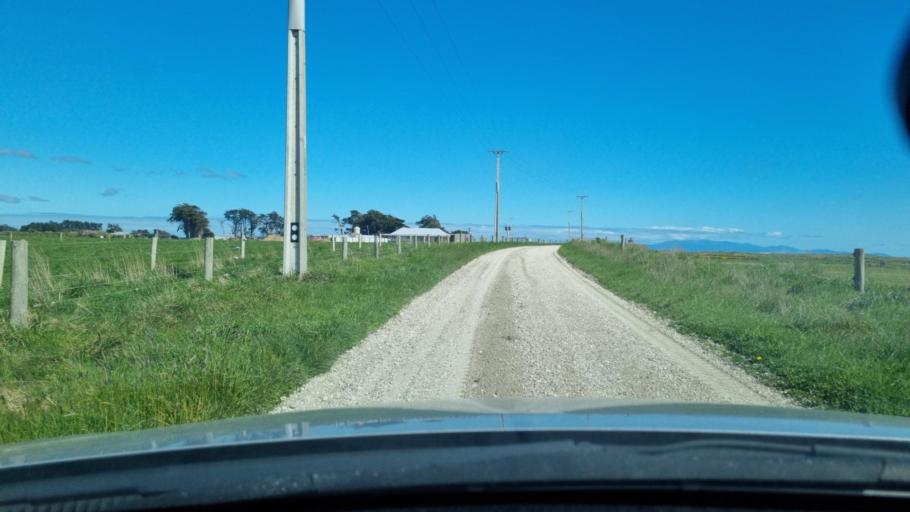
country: NZ
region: Southland
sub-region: Invercargill City
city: Invercargill
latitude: -46.3979
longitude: 168.2574
